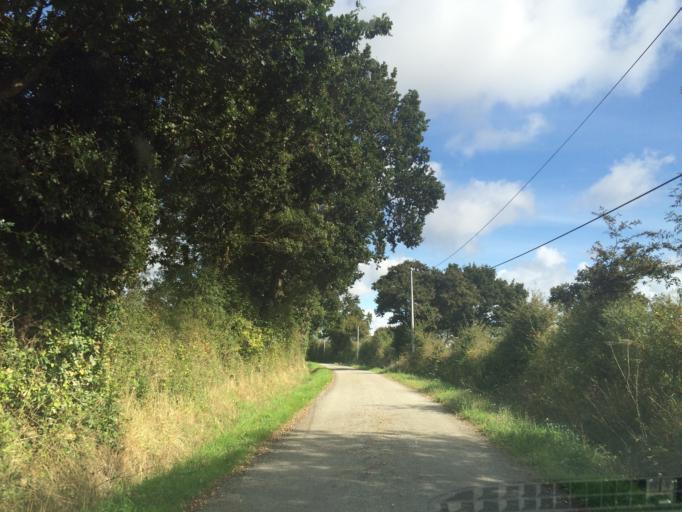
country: FR
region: Pays de la Loire
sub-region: Departement de la Loire-Atlantique
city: Chemere
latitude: 47.1221
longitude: -1.8902
